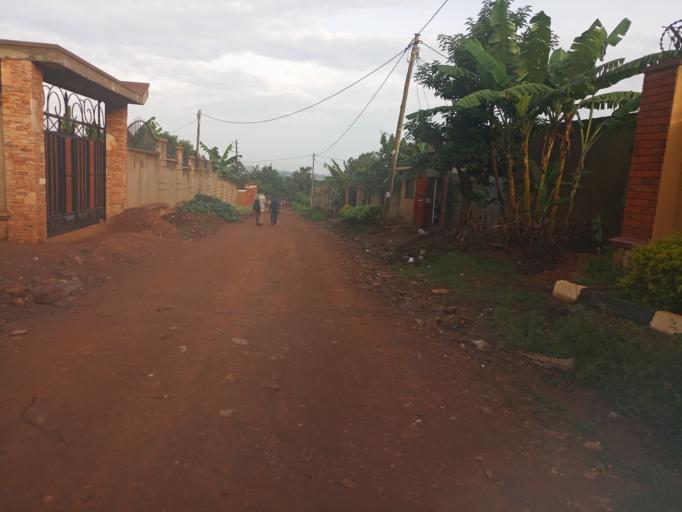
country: UG
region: Central Region
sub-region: Wakiso District
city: Kireka
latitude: 0.3936
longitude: 32.6358
